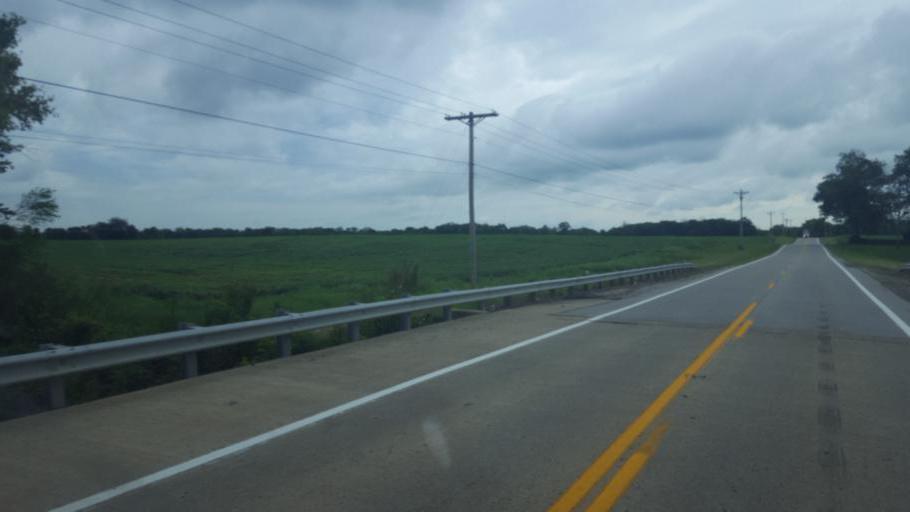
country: US
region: Ohio
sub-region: Pickaway County
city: Commercial Point
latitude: 39.7711
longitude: -83.0157
